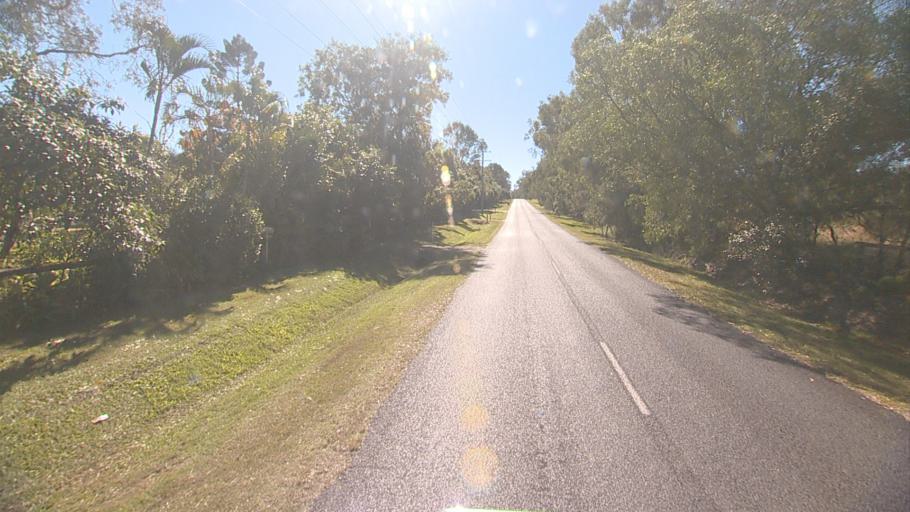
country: AU
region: Queensland
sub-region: Logan
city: Park Ridge South
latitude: -27.7164
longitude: 153.0578
